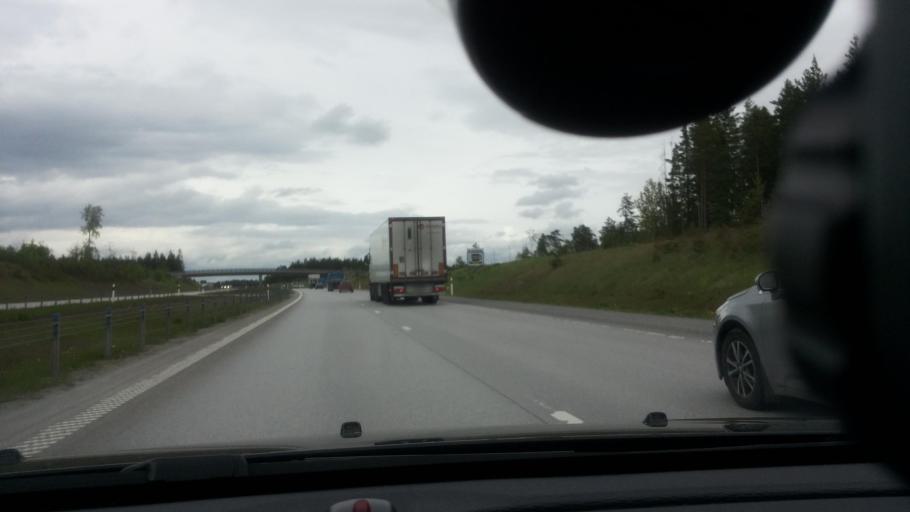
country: SE
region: Uppsala
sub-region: Uppsala Kommun
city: Gamla Uppsala
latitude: 59.9298
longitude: 17.6600
